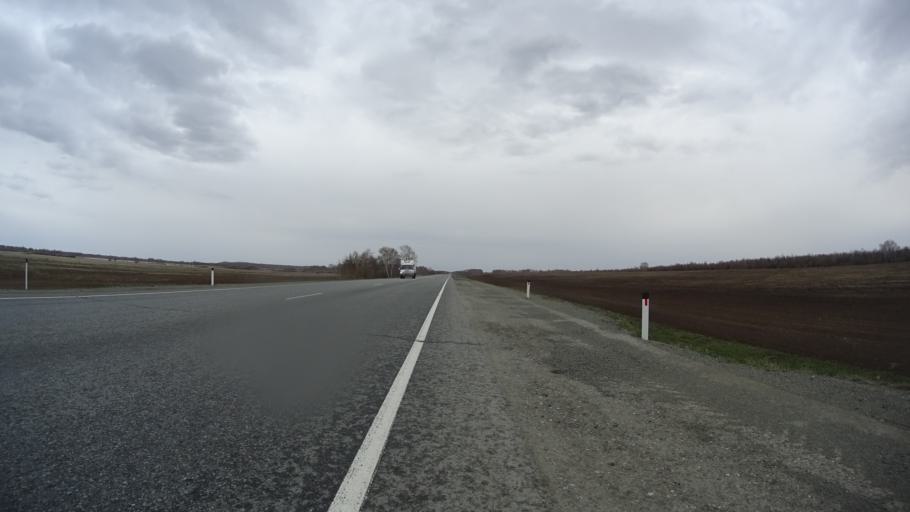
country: RU
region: Chelyabinsk
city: Krasnogorskiy
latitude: 54.6664
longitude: 61.2524
